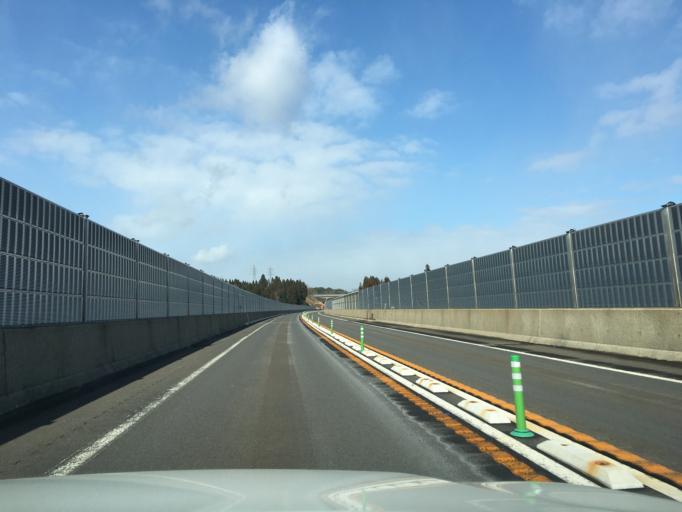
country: JP
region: Akita
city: Akita
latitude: 39.7547
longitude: 140.1395
